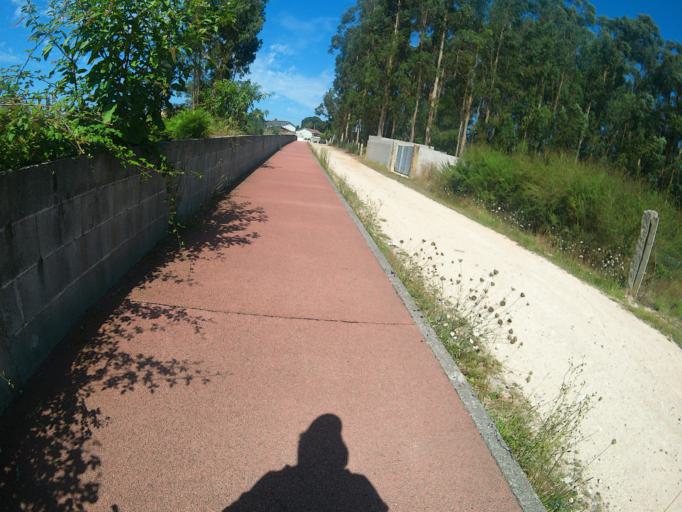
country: PT
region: Viana do Castelo
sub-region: Valenca
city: Valenca
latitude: 42.0123
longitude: -8.6528
